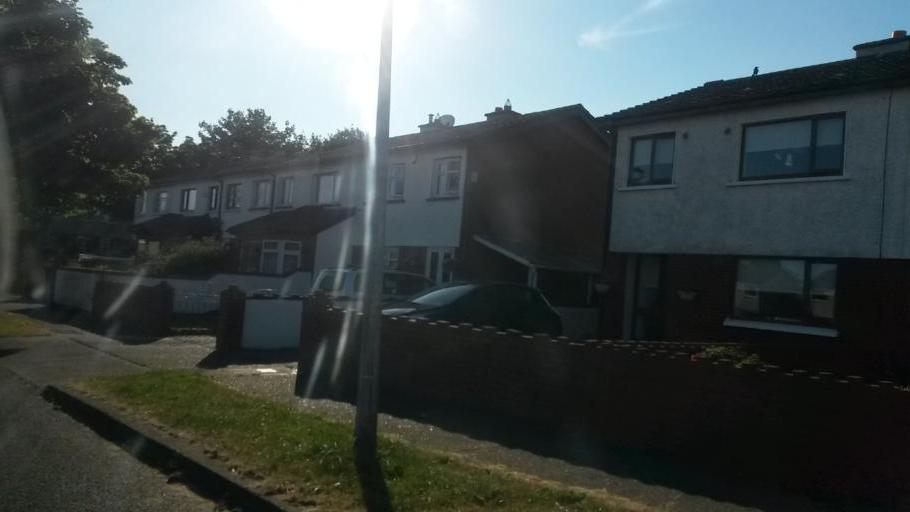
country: IE
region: Leinster
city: Ballymun
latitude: 53.4538
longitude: -6.2892
